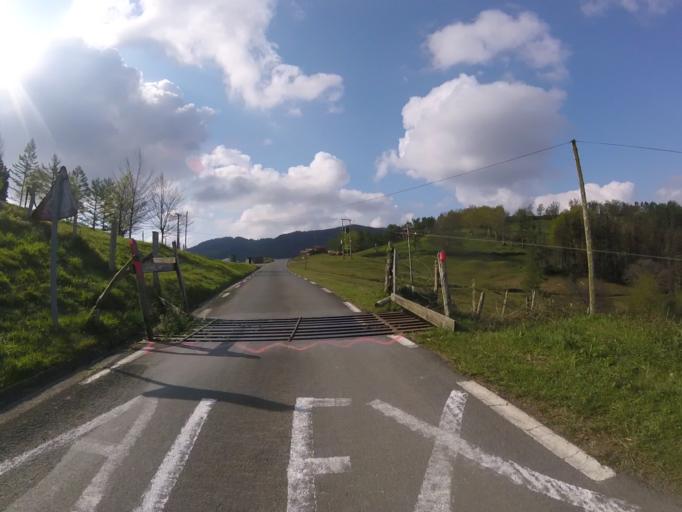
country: ES
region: Basque Country
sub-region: Provincia de Guipuzcoa
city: Azkoitia
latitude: 43.2191
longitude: -2.3108
